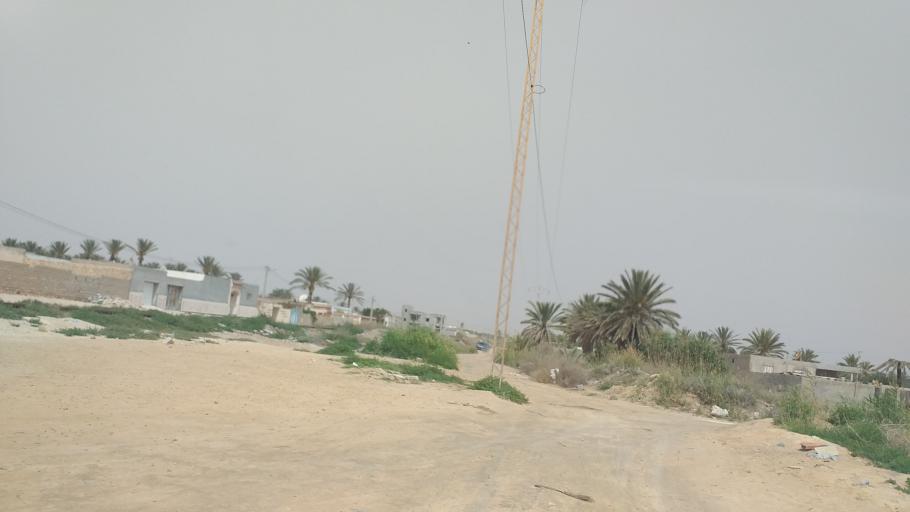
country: TN
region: Qabis
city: Gabes
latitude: 33.9420
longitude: 10.0557
